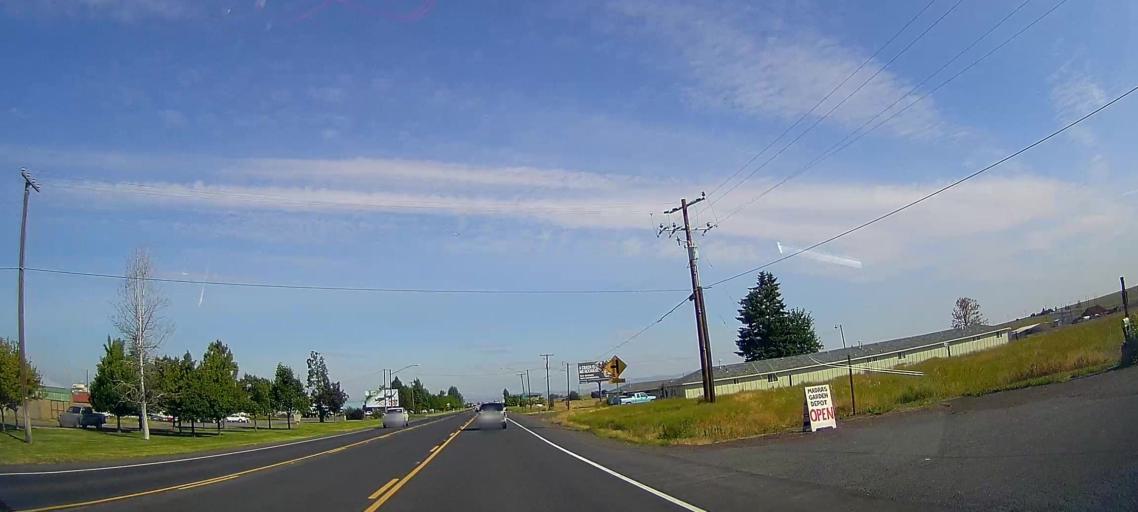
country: US
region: Oregon
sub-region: Jefferson County
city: Madras
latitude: 44.6600
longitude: -121.1325
